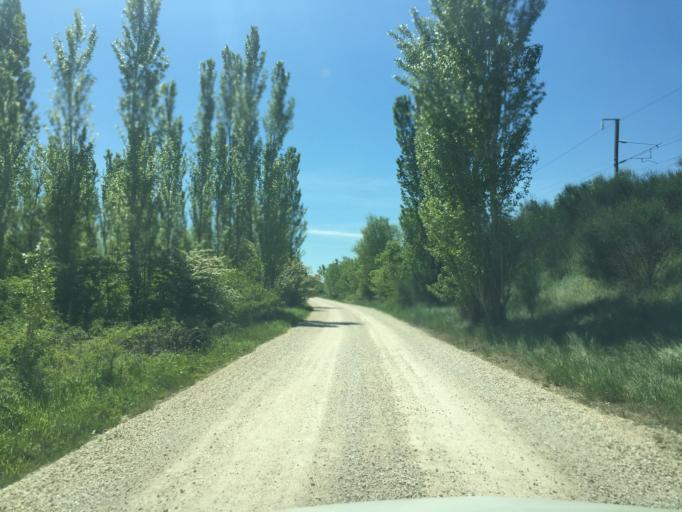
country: FR
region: Languedoc-Roussillon
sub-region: Departement du Gard
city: Montfaucon
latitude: 44.0845
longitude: 4.7716
